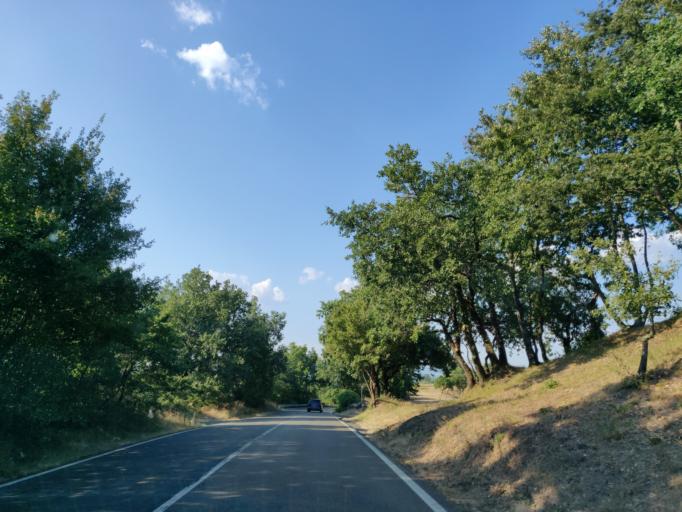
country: IT
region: Latium
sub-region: Provincia di Viterbo
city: Latera
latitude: 42.6354
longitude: 11.8363
